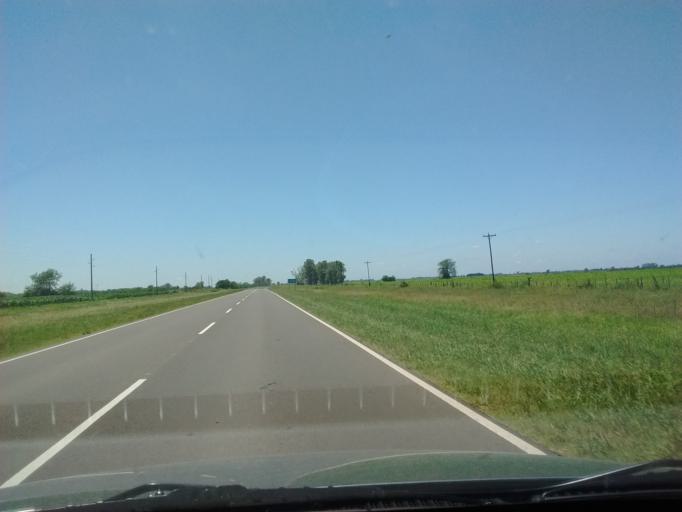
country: AR
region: Entre Rios
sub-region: Departamento de Gualeguay
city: Gualeguay
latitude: -33.0114
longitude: -59.4857
